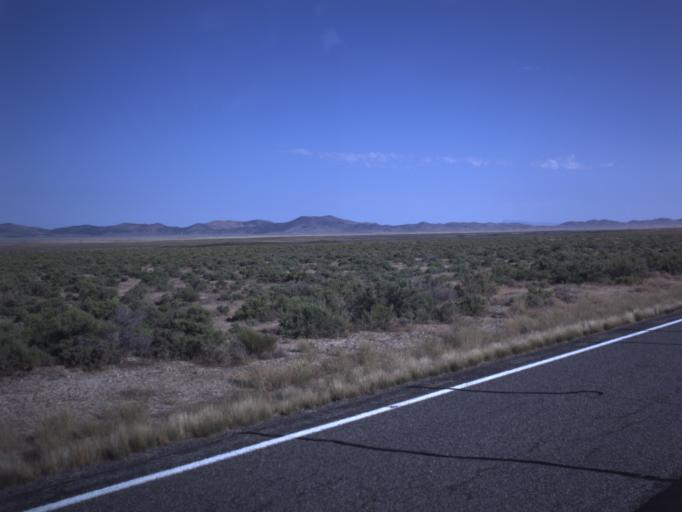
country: US
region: Utah
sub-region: Beaver County
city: Milford
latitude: 38.5073
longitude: -112.9911
